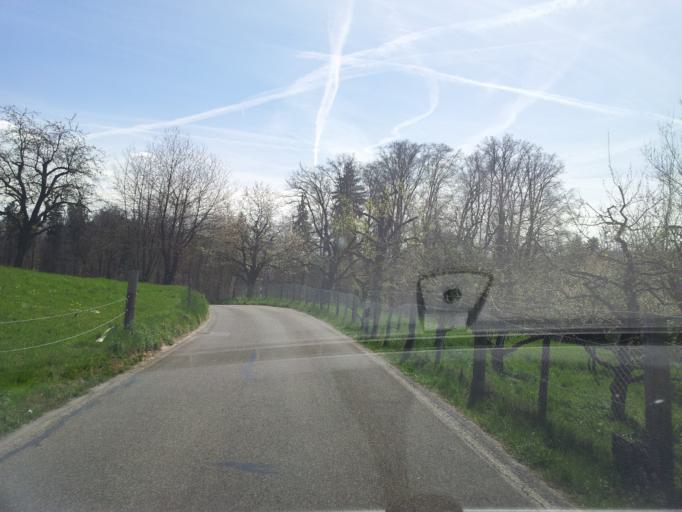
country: CH
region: Zurich
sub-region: Bezirk Dielsdorf
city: Daenikon
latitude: 47.4371
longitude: 8.3873
